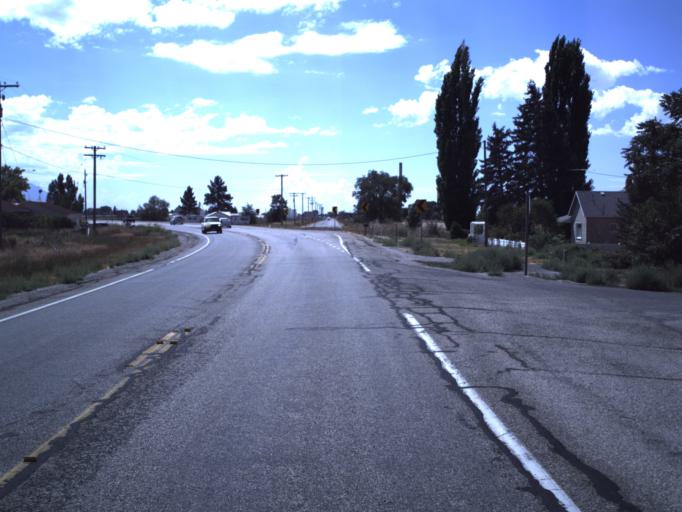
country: US
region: Utah
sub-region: Box Elder County
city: Garland
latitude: 41.7497
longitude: -112.1484
